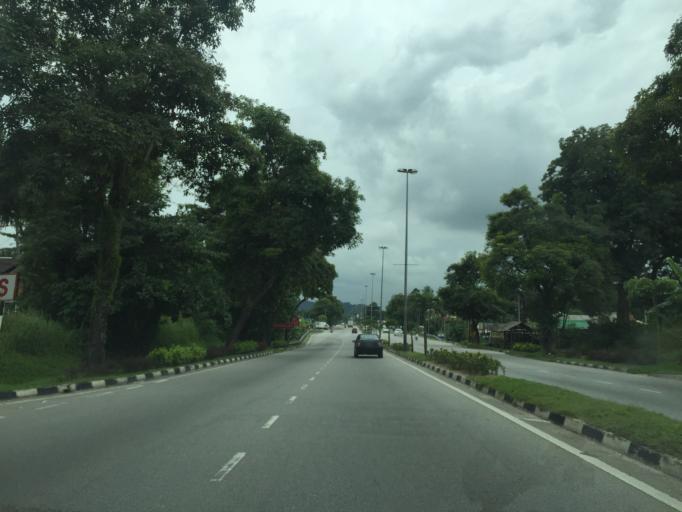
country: MY
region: Perak
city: Ipoh
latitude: 4.5420
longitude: 101.1219
